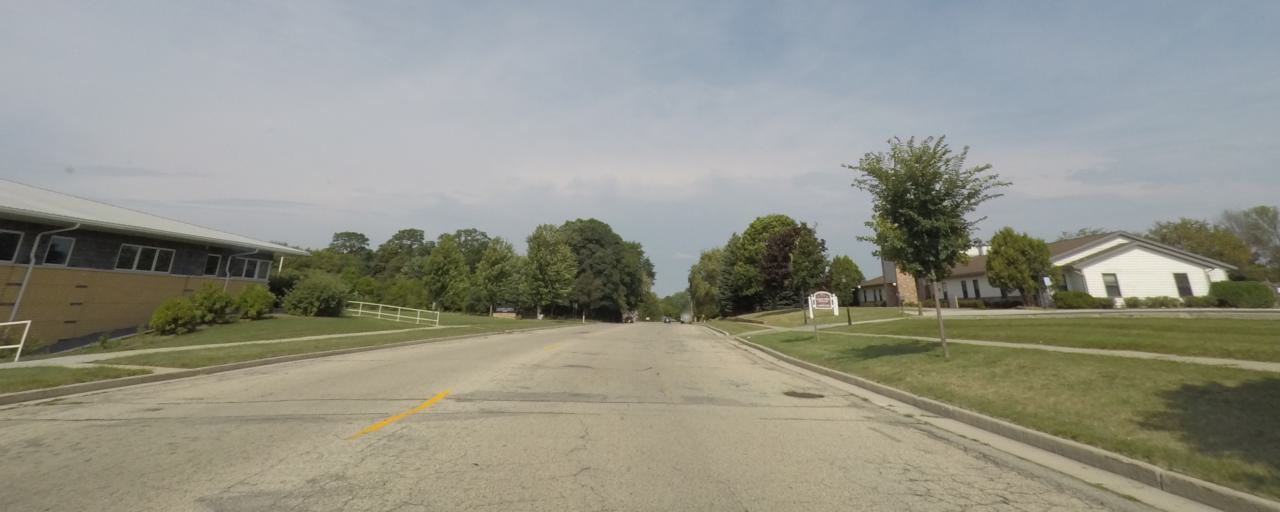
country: US
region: Wisconsin
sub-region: Jefferson County
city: Jefferson
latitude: 42.9908
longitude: -88.8234
